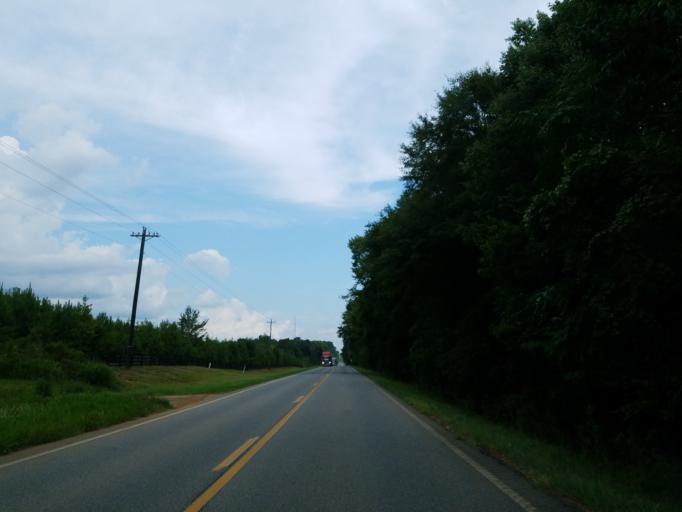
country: US
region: Georgia
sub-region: Dooly County
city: Unadilla
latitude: 32.3271
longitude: -83.7327
